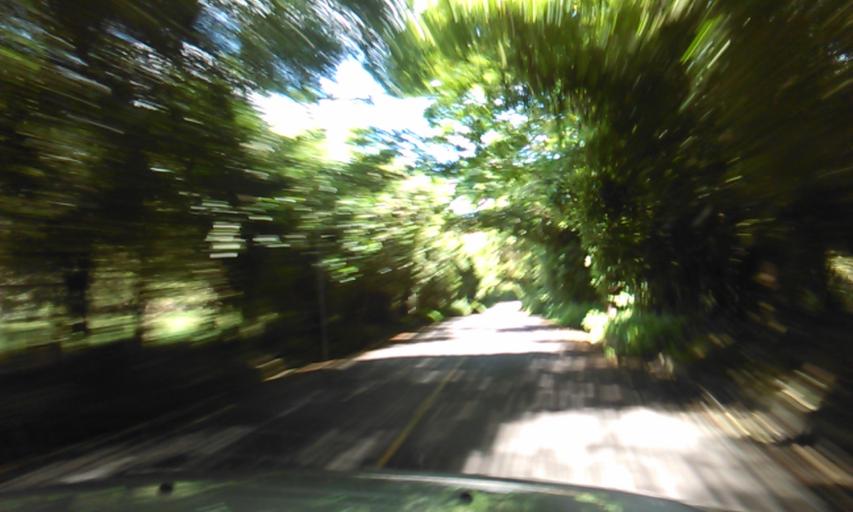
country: CO
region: Quindio
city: Cordoba
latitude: 4.4021
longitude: -75.7225
